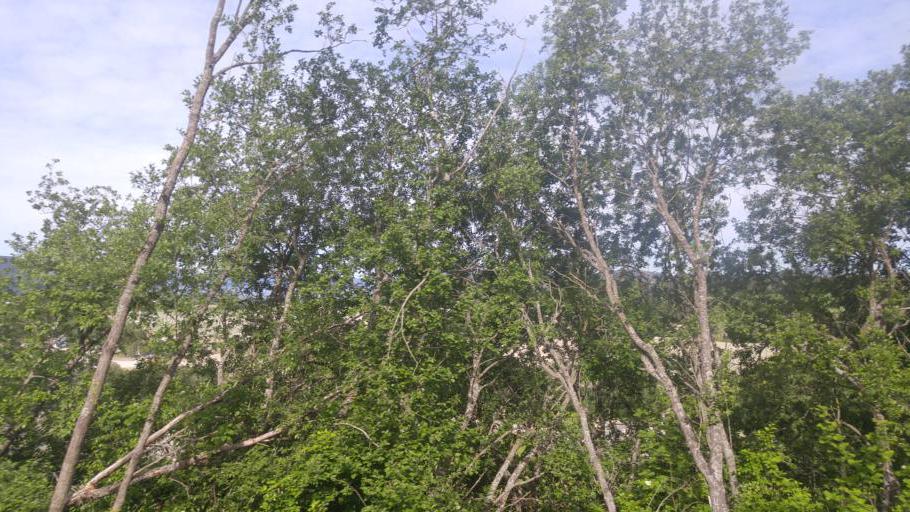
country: NO
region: Sor-Trondelag
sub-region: Melhus
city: Melhus
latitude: 63.3325
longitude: 10.3414
